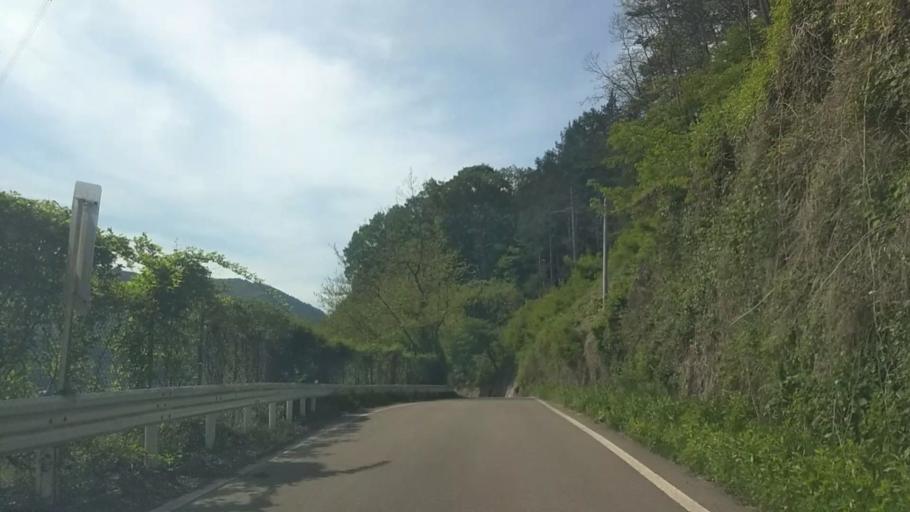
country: JP
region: Nagano
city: Saku
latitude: 36.1066
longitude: 138.4787
